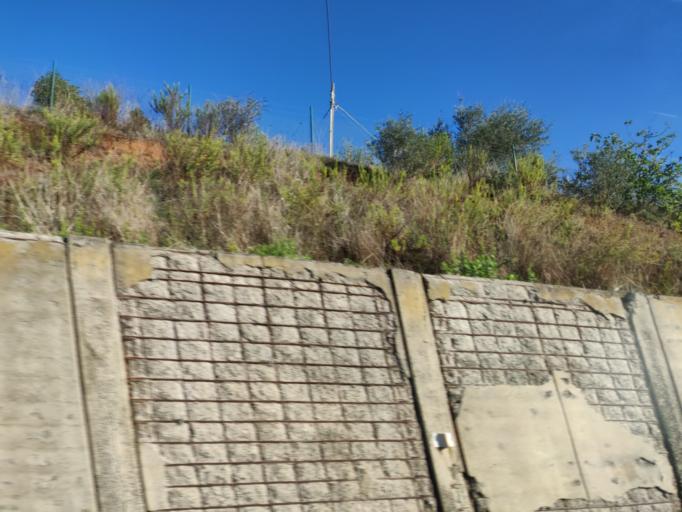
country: IT
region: Tuscany
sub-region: Provincia di Grosseto
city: Follonica
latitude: 42.9573
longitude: 10.7930
